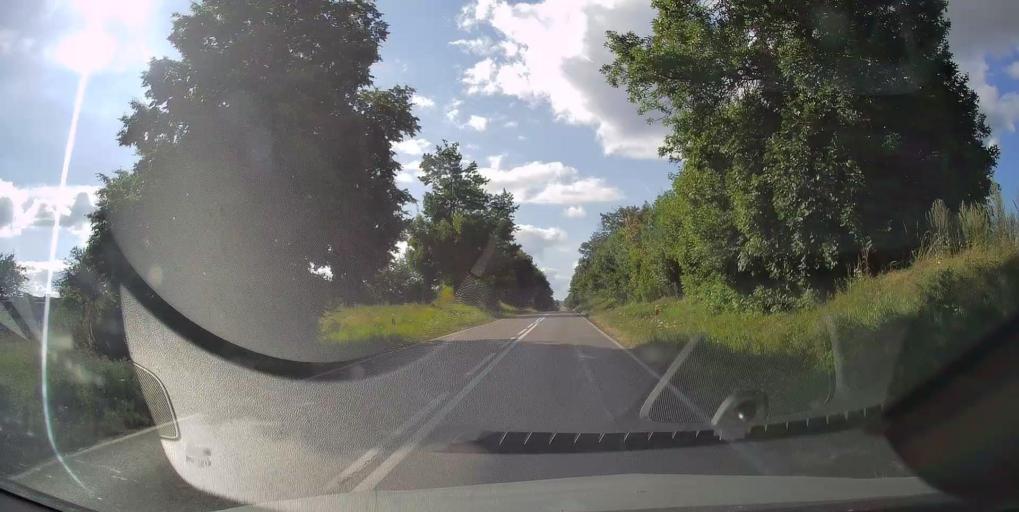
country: PL
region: Swietokrzyskie
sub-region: Powiat kielecki
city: Bodzentyn
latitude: 50.9663
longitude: 20.8917
